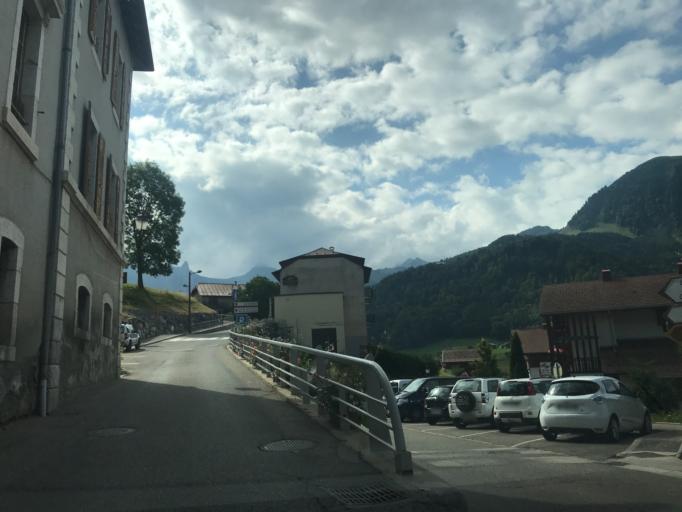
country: FR
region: Rhone-Alpes
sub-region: Departement de la Haute-Savoie
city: Thones
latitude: 45.8611
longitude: 6.3695
